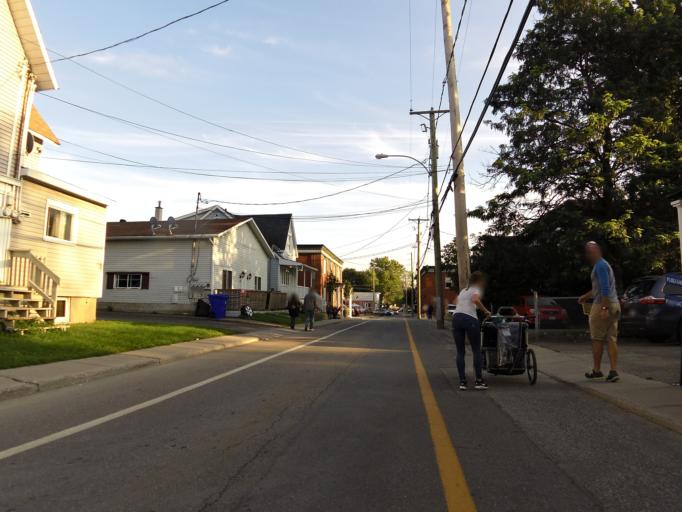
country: CA
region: Quebec
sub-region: Outaouais
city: Gatineau
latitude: 45.4587
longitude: -75.6983
